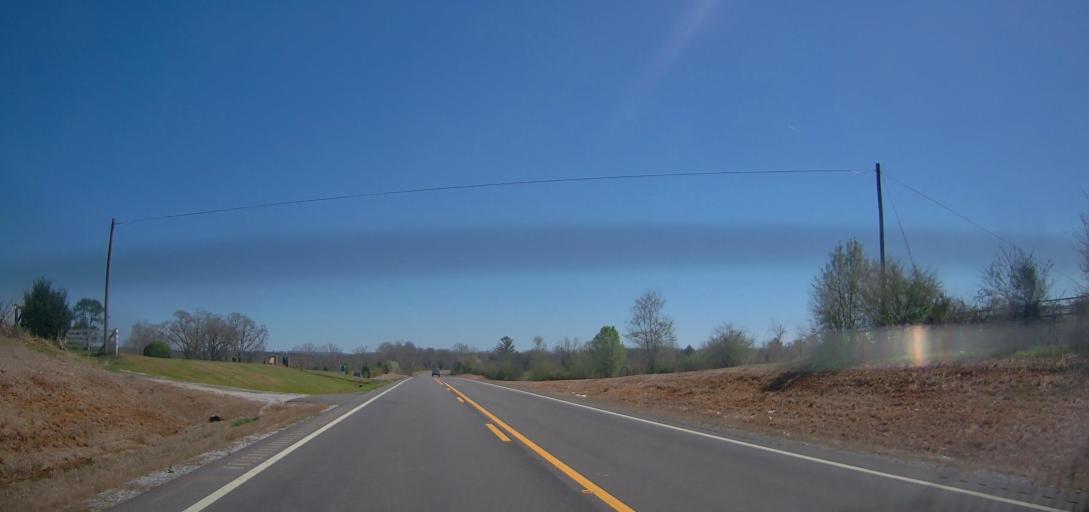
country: US
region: Alabama
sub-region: Calhoun County
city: Alexandria
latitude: 33.7846
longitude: -85.9326
